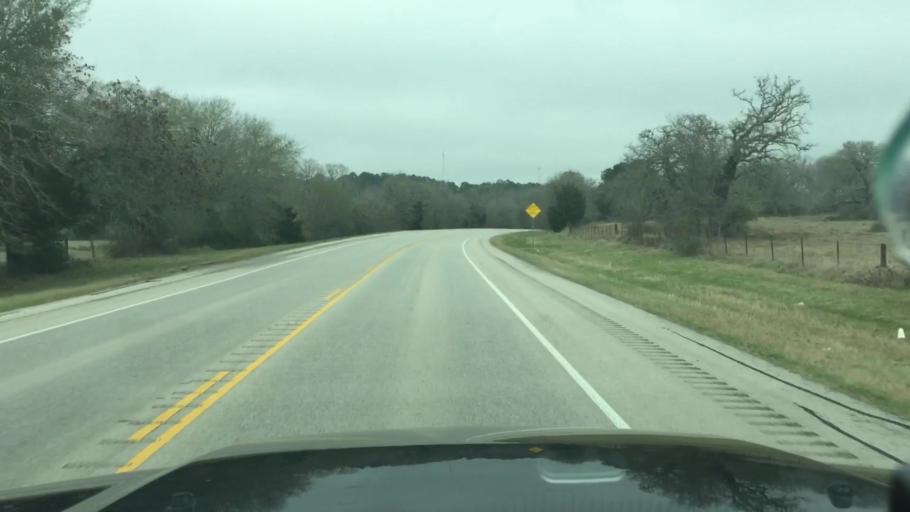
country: US
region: Texas
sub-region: Fayette County
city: La Grange
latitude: 30.0319
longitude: -96.9080
